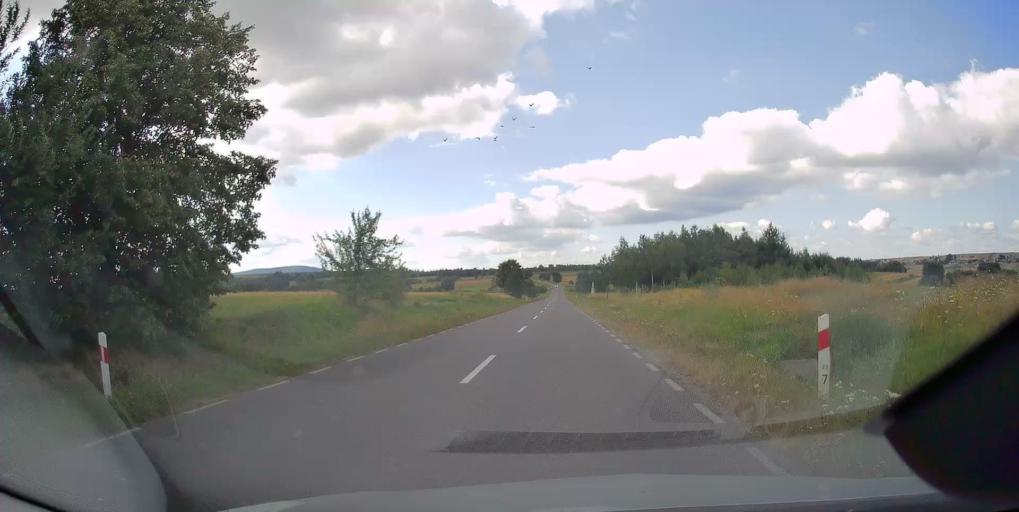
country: PL
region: Swietokrzyskie
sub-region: Powiat kielecki
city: Nowa Slupia
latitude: 50.8961
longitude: 21.0215
